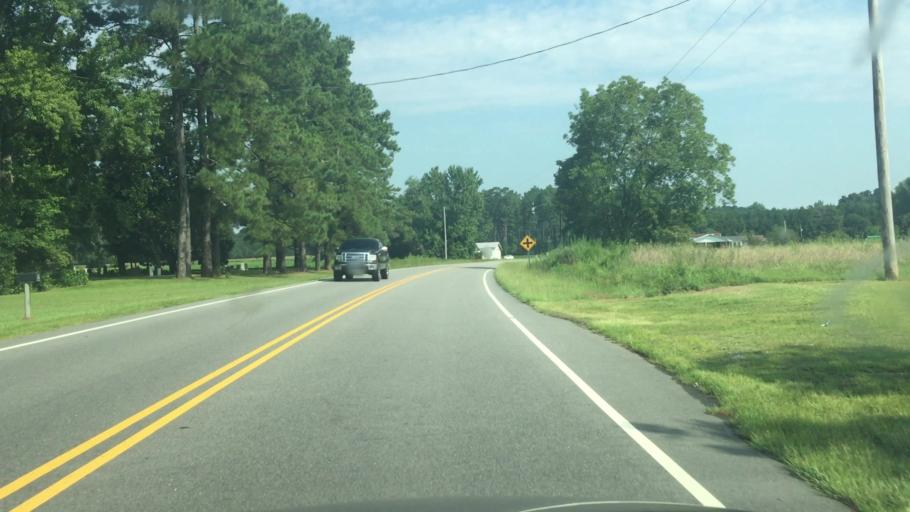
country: US
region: North Carolina
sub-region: Columbus County
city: Chadbourn
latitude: 34.2917
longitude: -78.8255
